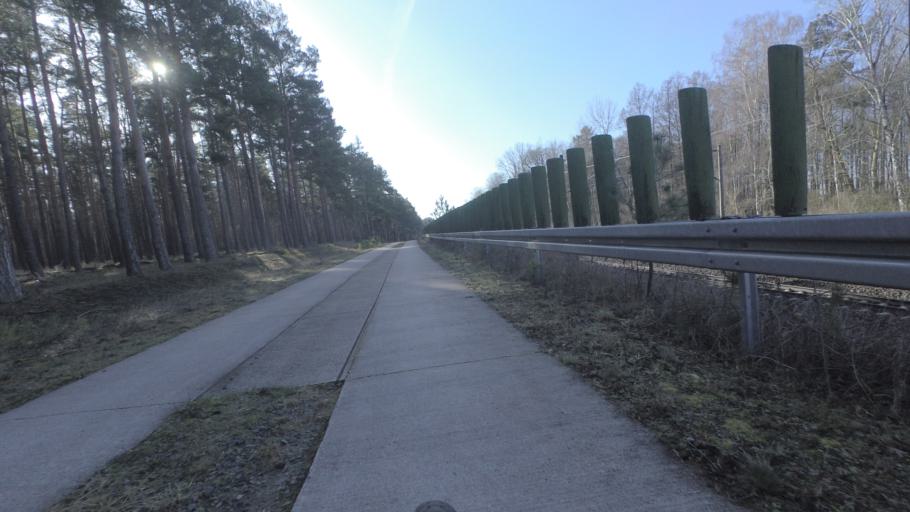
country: DE
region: Brandenburg
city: Luckenwalde
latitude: 52.1394
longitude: 13.2187
